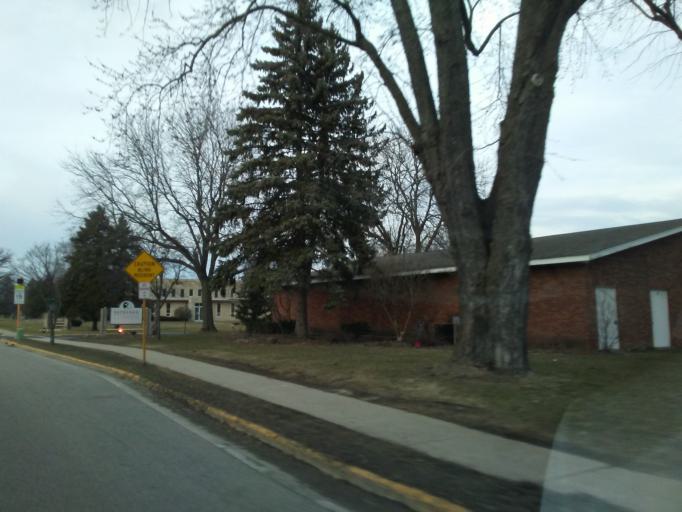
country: US
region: Wisconsin
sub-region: Dane County
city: Verona
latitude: 42.9933
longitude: -89.5335
